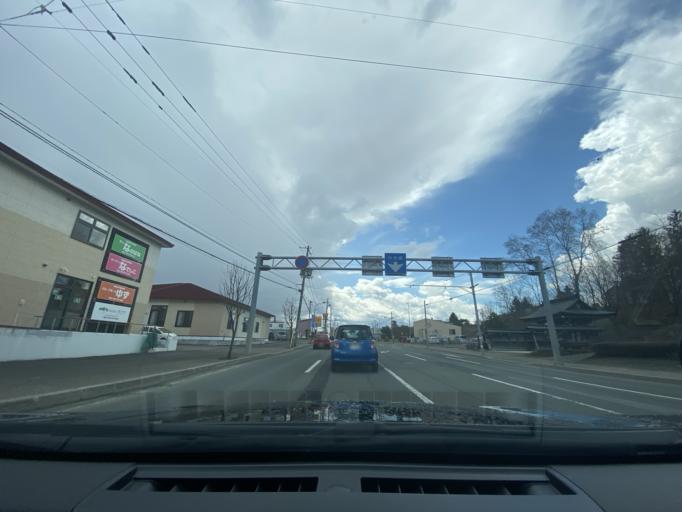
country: JP
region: Hokkaido
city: Kitami
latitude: 43.8147
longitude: 143.9057
